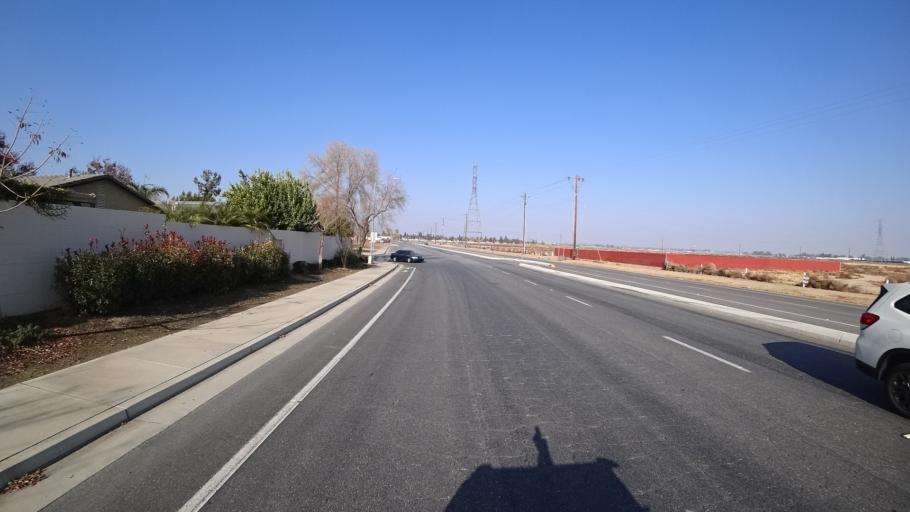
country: US
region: California
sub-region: Kern County
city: Greenacres
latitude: 35.3958
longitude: -119.0657
